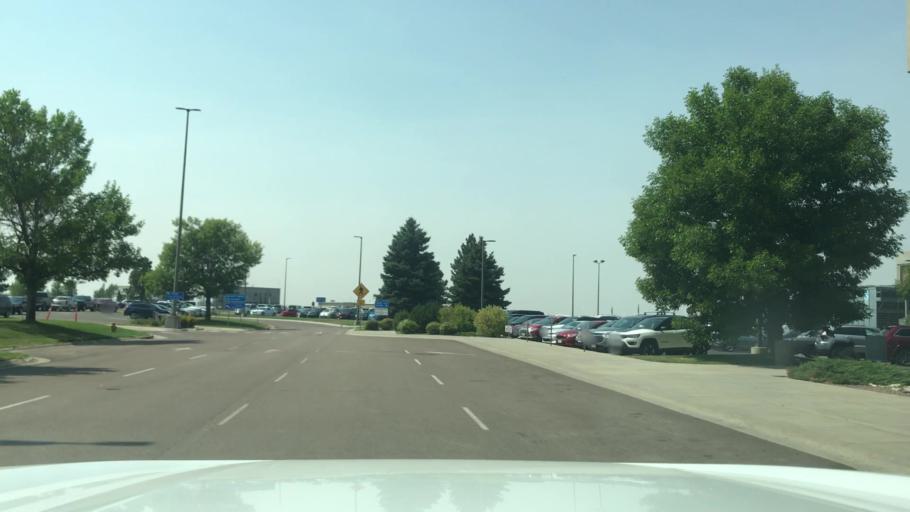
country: US
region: Montana
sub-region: Cascade County
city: Great Falls
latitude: 47.4819
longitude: -111.3570
